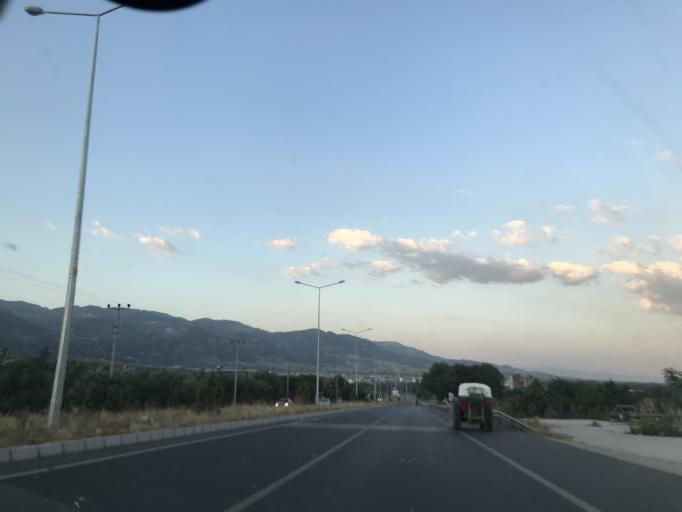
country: TR
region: Aydin
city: Buharkent
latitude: 37.9575
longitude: 28.7100
